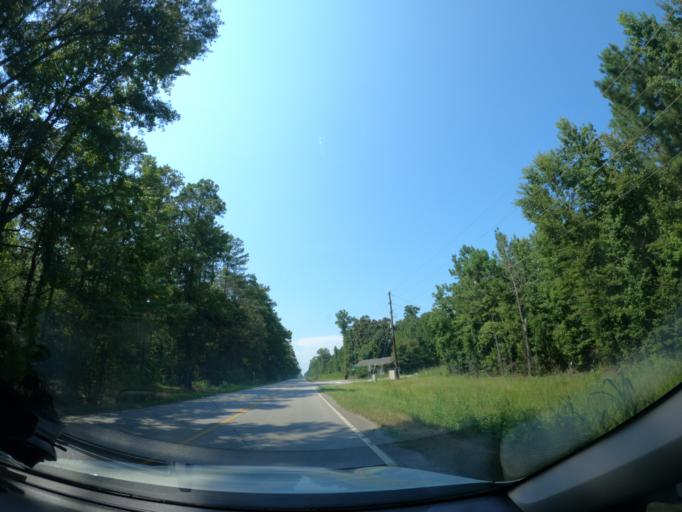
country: US
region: South Carolina
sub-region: Richland County
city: Hopkins
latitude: 33.8734
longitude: -80.8972
